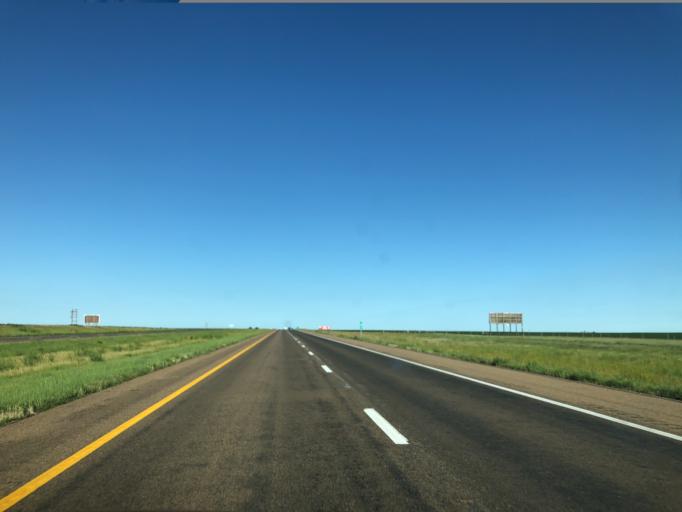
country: US
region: Kansas
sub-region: Thomas County
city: Colby
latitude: 39.3660
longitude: -101.1831
